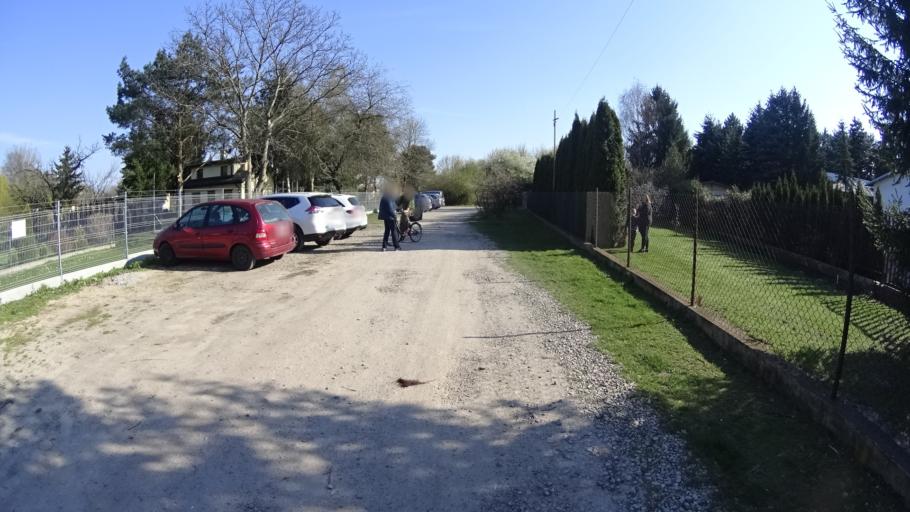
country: PL
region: Masovian Voivodeship
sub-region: Warszawa
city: Bemowo
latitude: 52.2465
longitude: 20.8912
